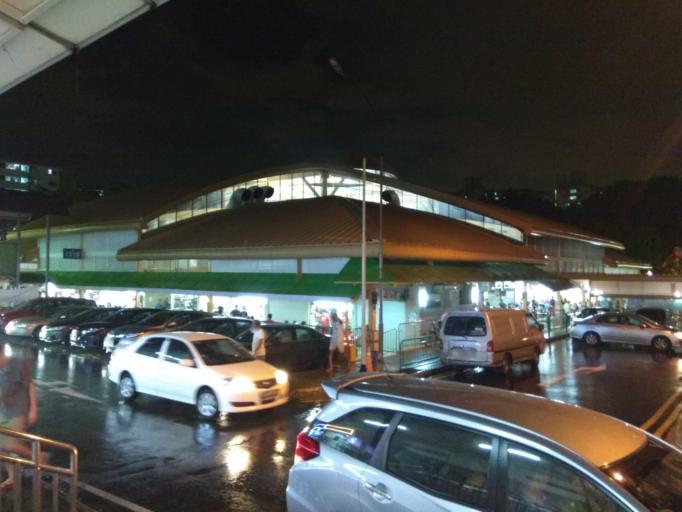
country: MY
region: Johor
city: Johor Bahru
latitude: 1.3456
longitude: 103.7128
